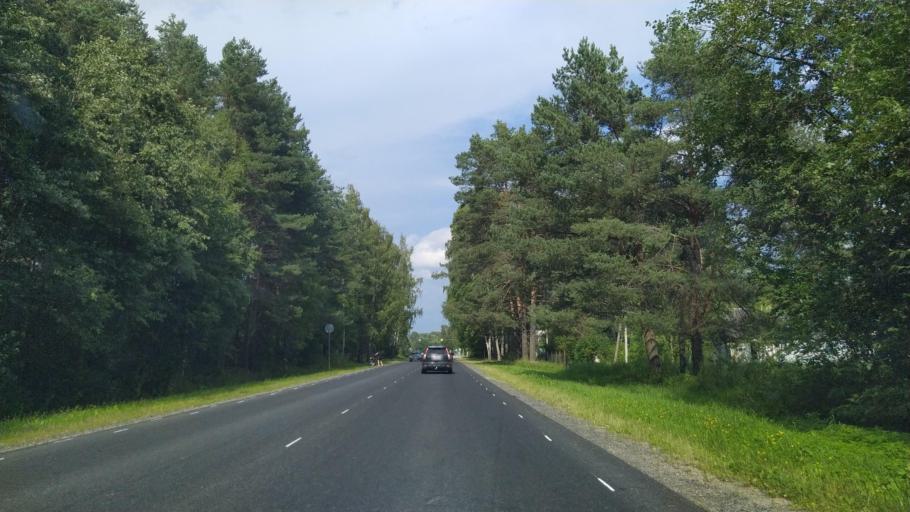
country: RU
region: Pskov
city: Porkhov
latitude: 57.8479
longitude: 29.5476
